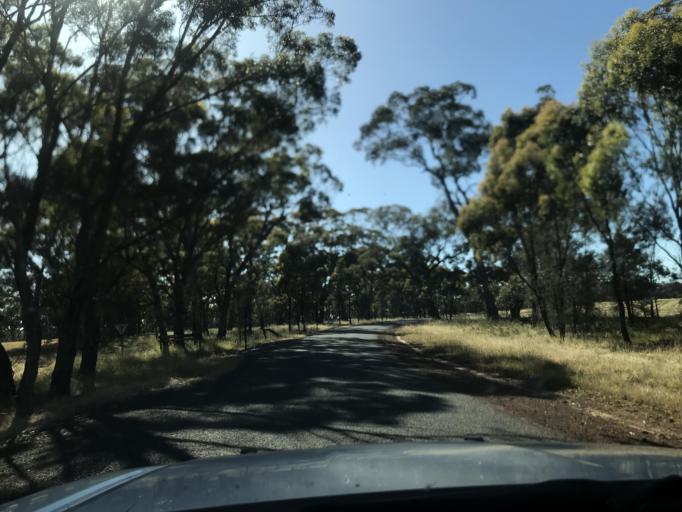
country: AU
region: Victoria
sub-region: Horsham
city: Horsham
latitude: -37.0124
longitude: 141.6714
